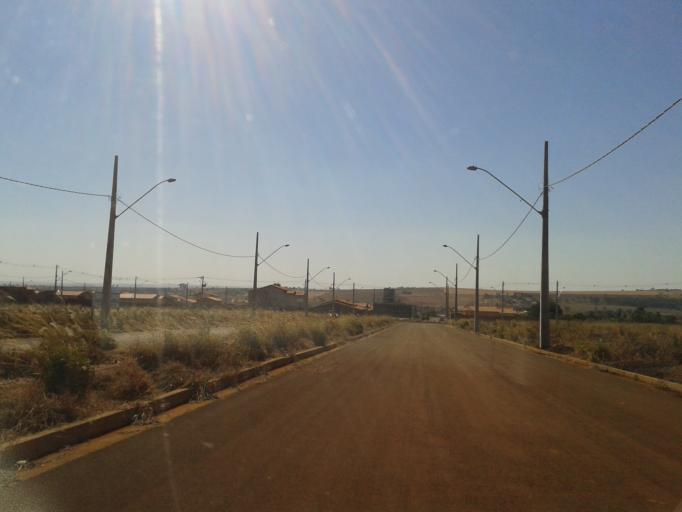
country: BR
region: Minas Gerais
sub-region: Capinopolis
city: Capinopolis
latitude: -18.6949
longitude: -49.5757
